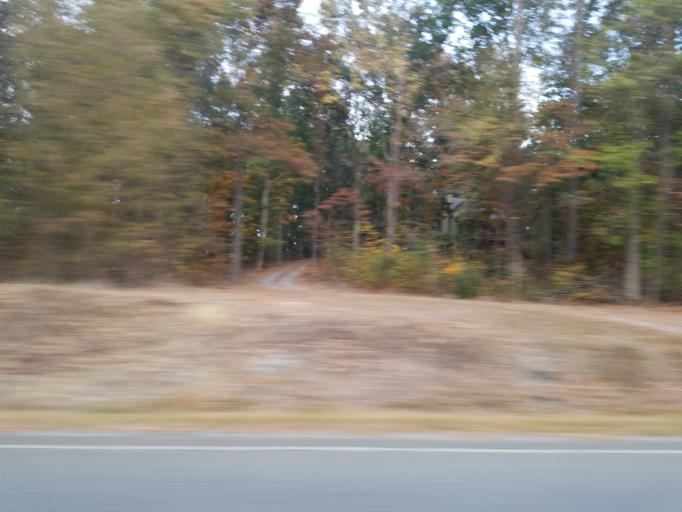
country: US
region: Georgia
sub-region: Murray County
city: Chatsworth
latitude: 34.5894
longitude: -84.7214
